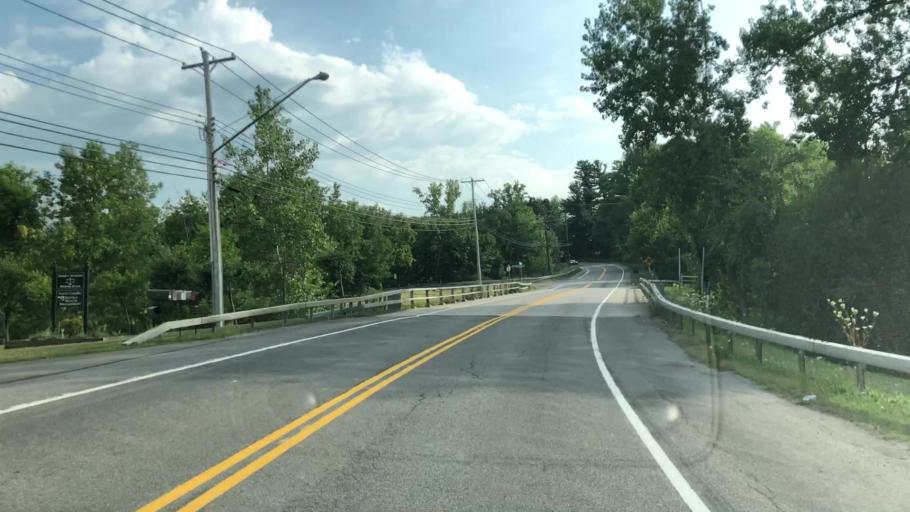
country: US
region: New York
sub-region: Erie County
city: Elma Center
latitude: 42.8490
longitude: -78.6405
